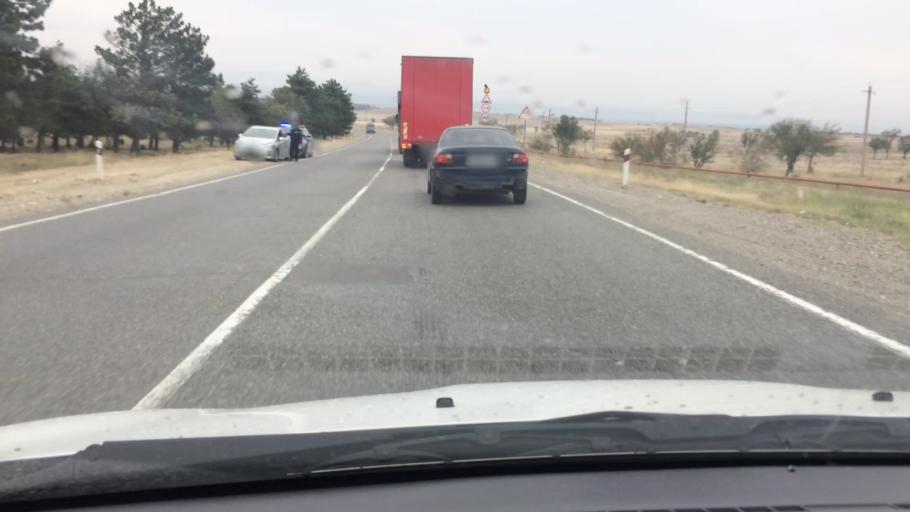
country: GE
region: T'bilisi
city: Tbilisi
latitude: 41.6387
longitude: 44.8722
